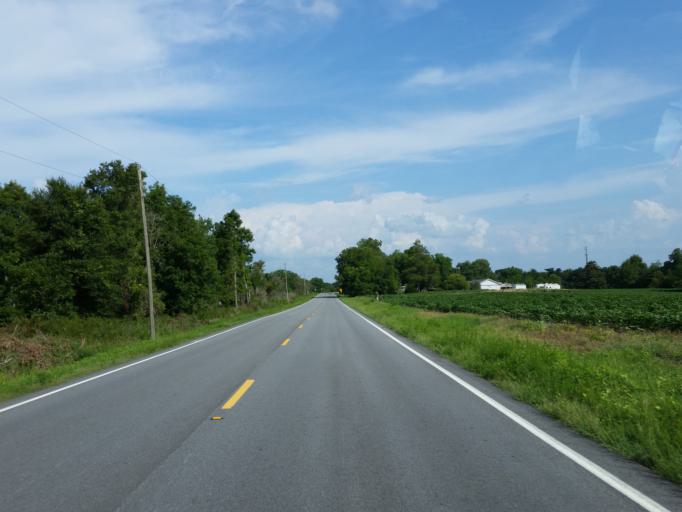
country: US
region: Georgia
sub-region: Turner County
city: Ashburn
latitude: 31.8084
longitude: -83.7167
